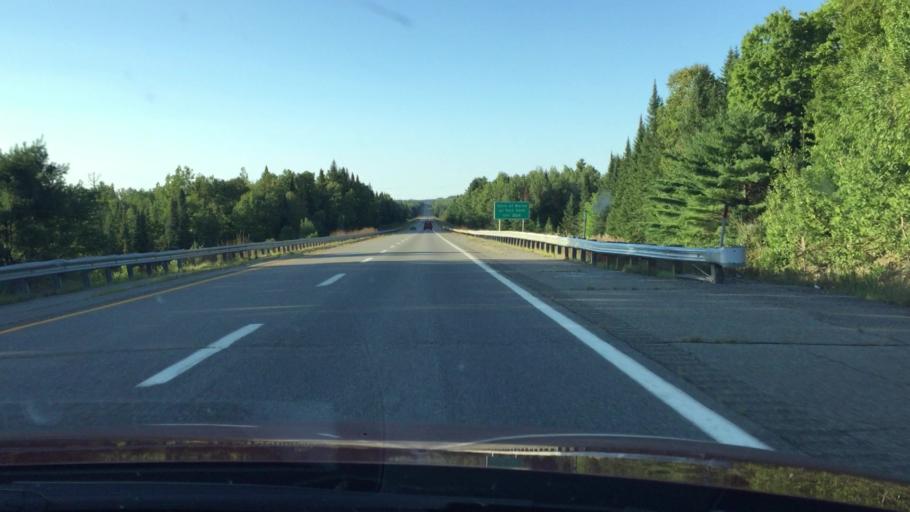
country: US
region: Maine
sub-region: Penobscot County
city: Patten
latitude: 45.8111
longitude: -68.4286
